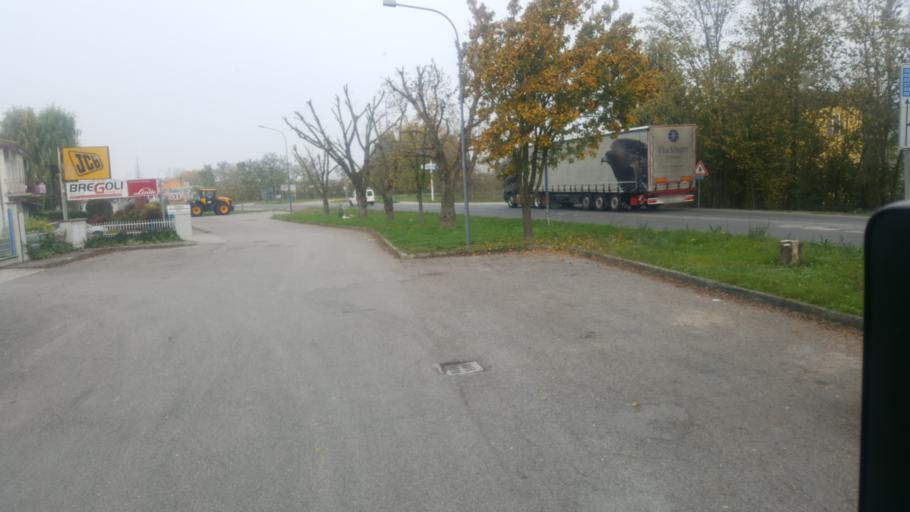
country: IT
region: Emilia-Romagna
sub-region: Provincia di Ferrara
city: Bondeno
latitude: 44.8982
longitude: 11.4053
